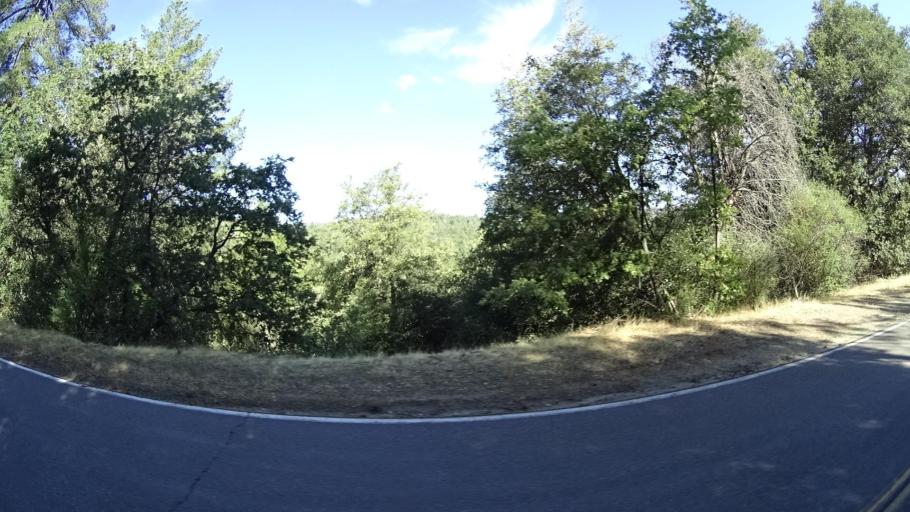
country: US
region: California
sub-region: Riverside County
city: Aguanga
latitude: 33.2870
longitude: -116.8000
